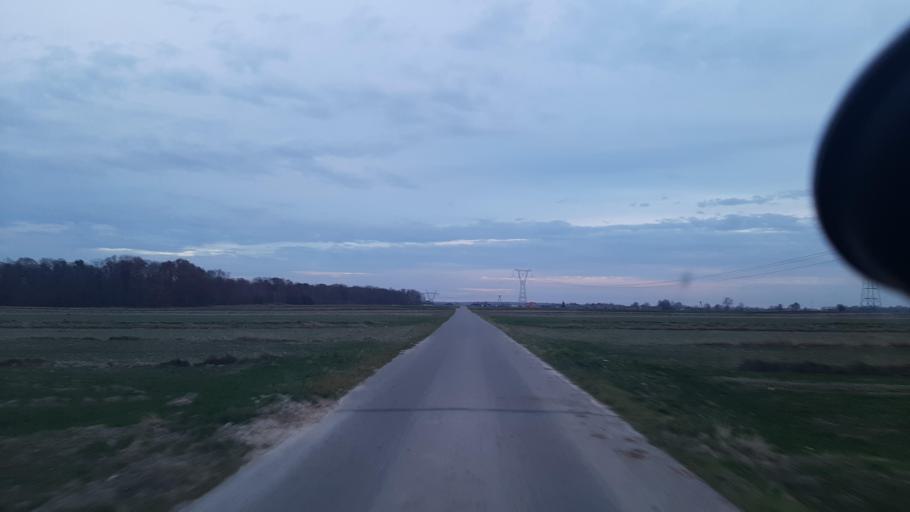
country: PL
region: Lublin Voivodeship
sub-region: Powiat lubelski
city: Garbow
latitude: 51.3744
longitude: 22.3748
